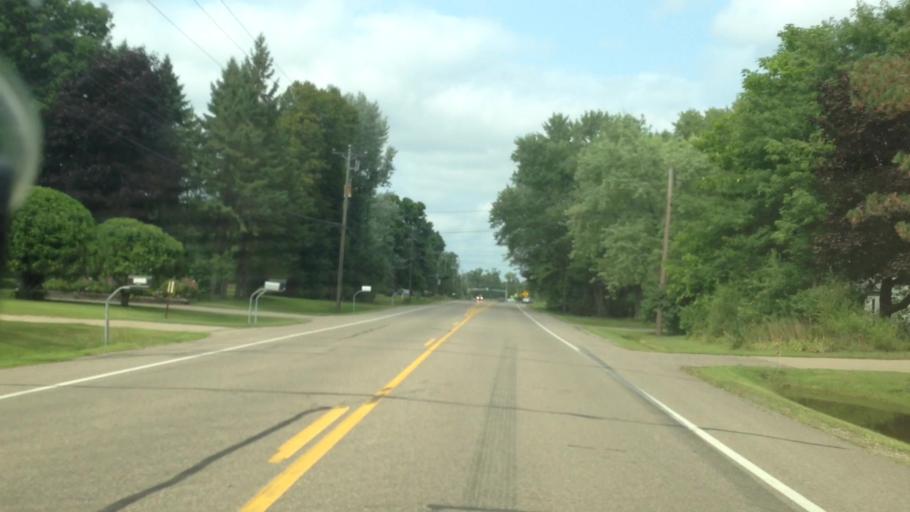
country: US
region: Minnesota
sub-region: Anoka County
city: Circle Pines
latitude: 45.1374
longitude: -93.1271
